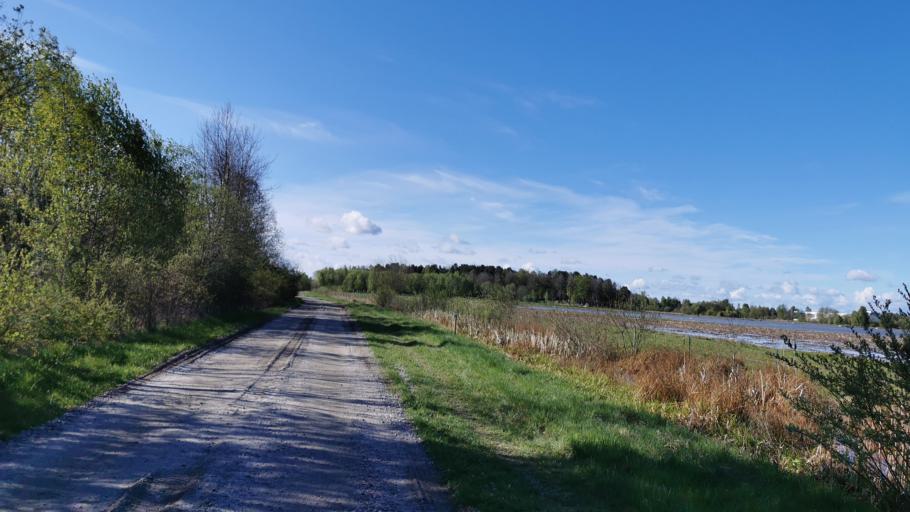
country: SE
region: OErebro
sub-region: Orebro Kommun
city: Orebro
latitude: 59.3026
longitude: 15.2208
